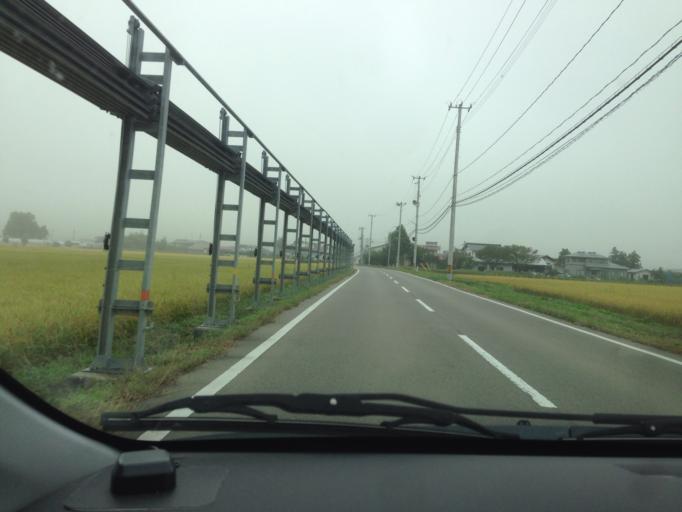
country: JP
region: Fukushima
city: Kitakata
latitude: 37.5639
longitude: 139.8532
